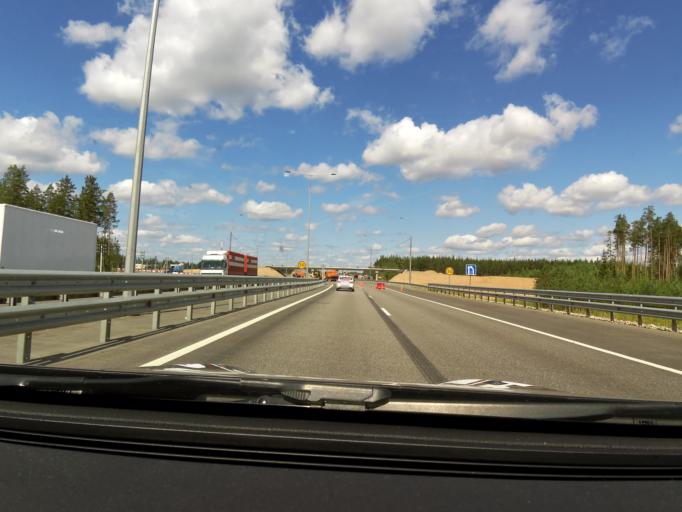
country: RU
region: Tverskaya
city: Bologoye
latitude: 57.6993
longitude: 34.2057
